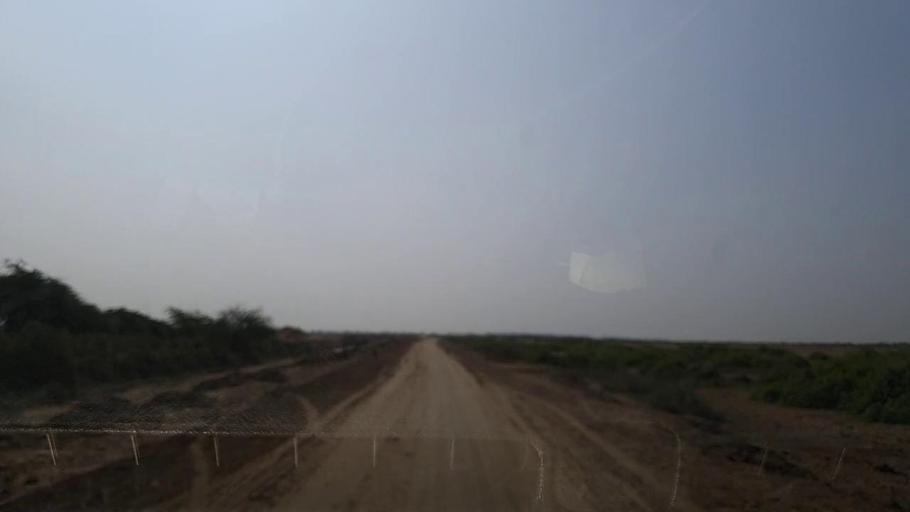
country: PK
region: Sindh
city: Mirpur Sakro
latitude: 24.5403
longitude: 67.7857
